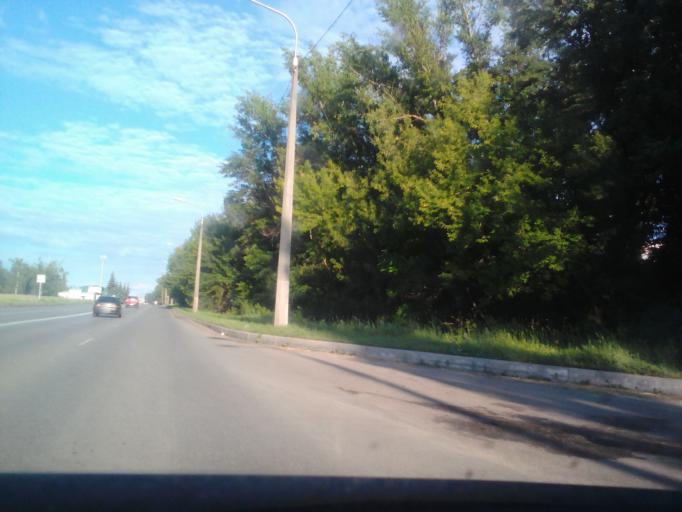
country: RU
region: Kursk
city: Kurchatov
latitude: 51.6574
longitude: 35.6512
